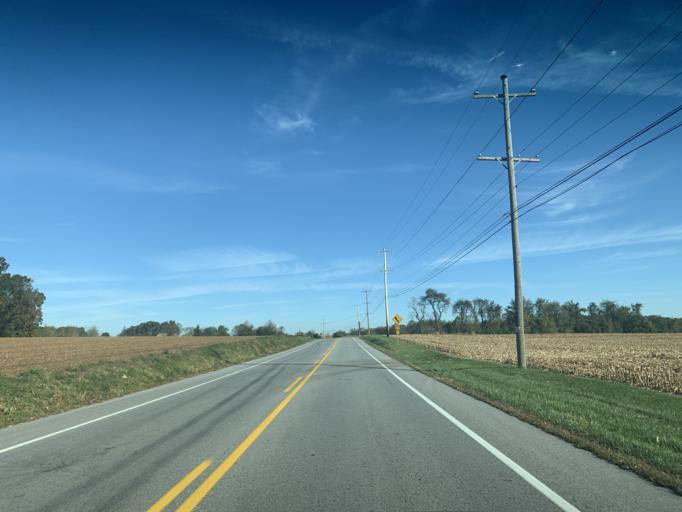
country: US
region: Pennsylvania
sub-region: Chester County
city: Parkesburg
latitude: 39.9227
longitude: -75.9151
